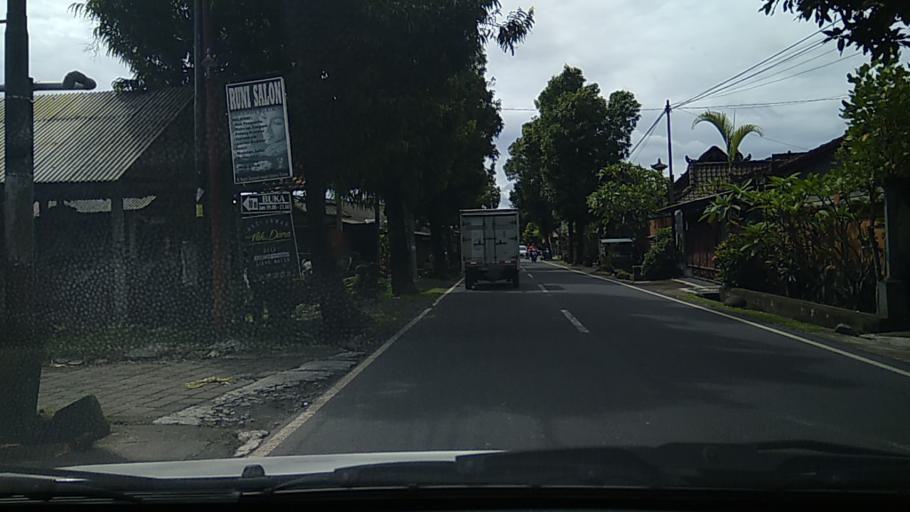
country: ID
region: Bali
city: Banjar Sedang
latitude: -8.5725
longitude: 115.2568
